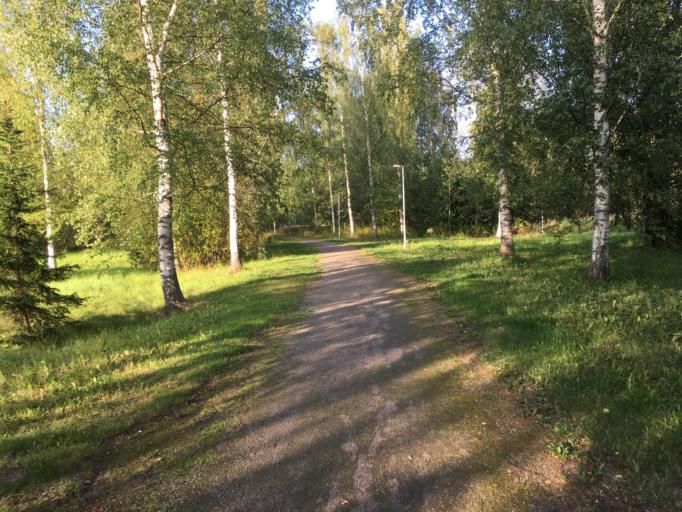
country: FI
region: Central Finland
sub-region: Jyvaeskylae
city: Jyvaeskylae
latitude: 62.2242
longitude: 25.7918
